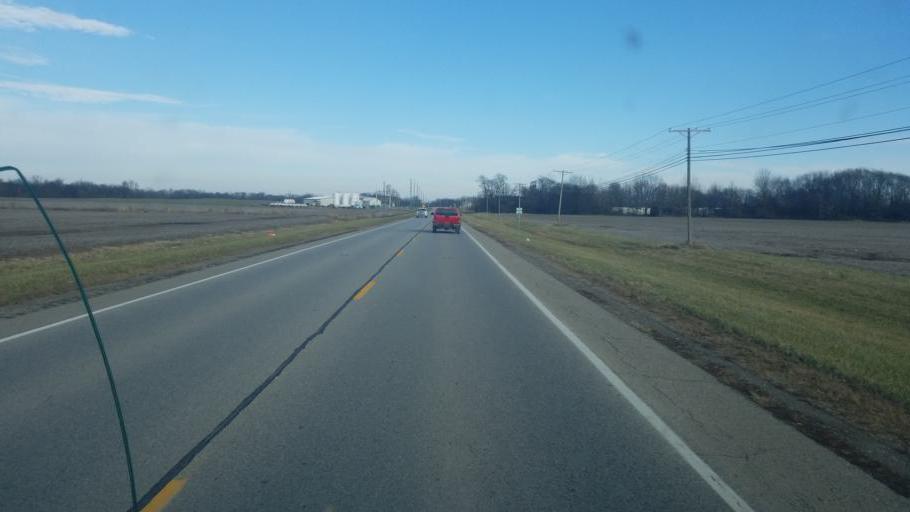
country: US
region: Illinois
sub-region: White County
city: Carmi
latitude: 38.1030
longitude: -88.1379
